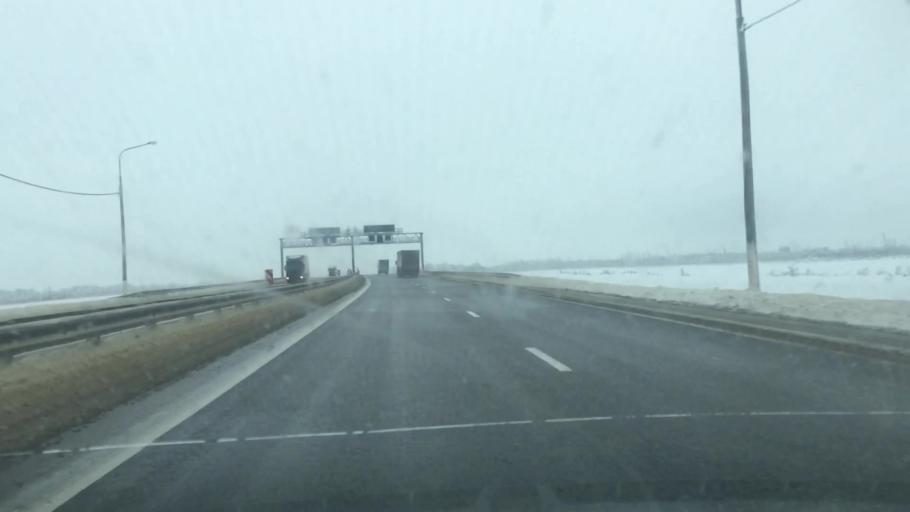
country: RU
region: Lipetsk
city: Stanovoye
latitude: 52.8966
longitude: 38.2278
